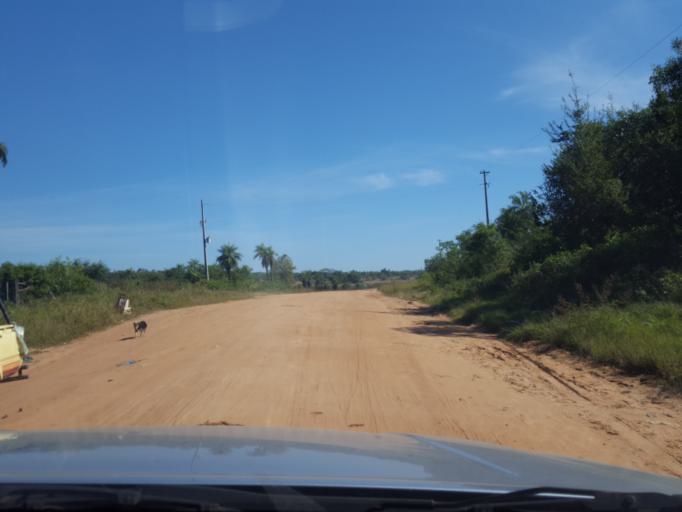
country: PY
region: Cordillera
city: Tobati
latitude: -25.2571
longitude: -57.0956
